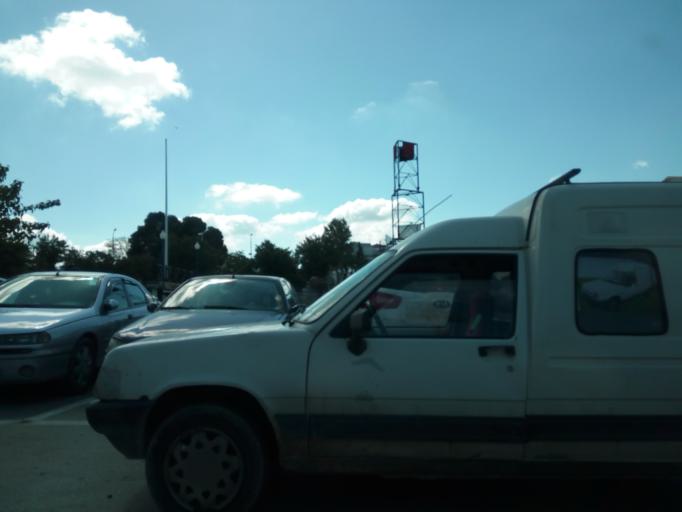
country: DZ
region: Constantine
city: Constantine
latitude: 36.3648
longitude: 6.6078
